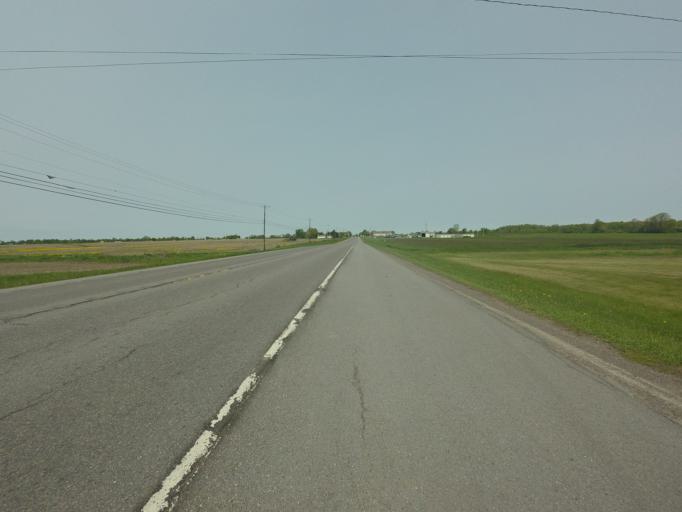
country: US
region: New York
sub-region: Jefferson County
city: Dexter
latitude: 44.0562
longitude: -76.1103
